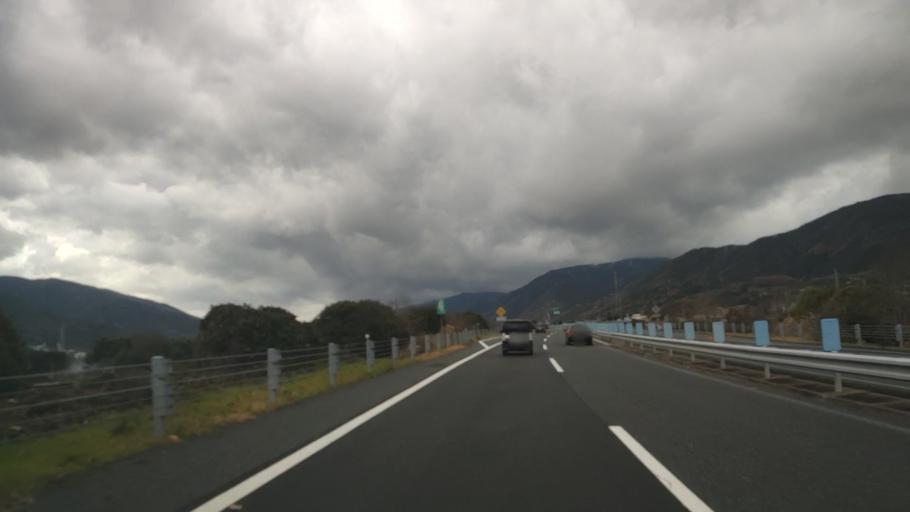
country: JP
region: Tokushima
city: Ikedacho
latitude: 34.0368
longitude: 133.9003
